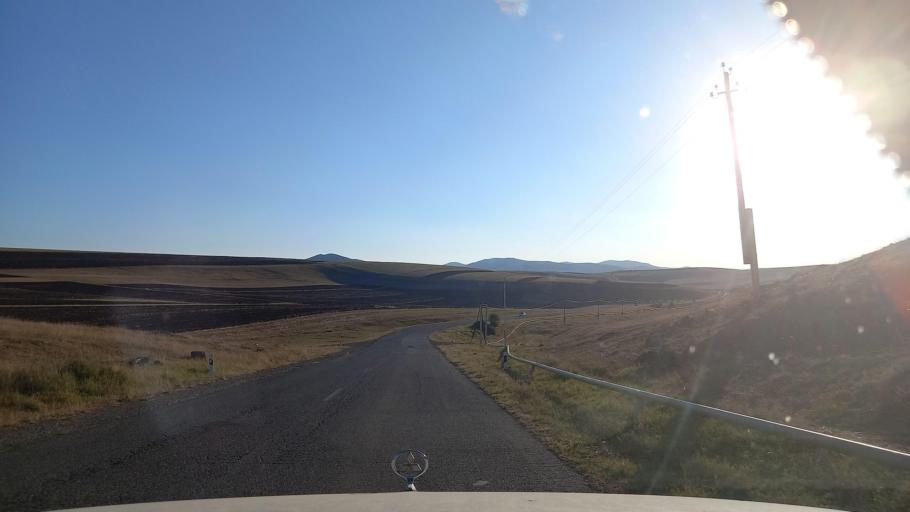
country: AZ
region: Shamkir Rayon
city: Shamkhor
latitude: 40.7649
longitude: 45.9346
